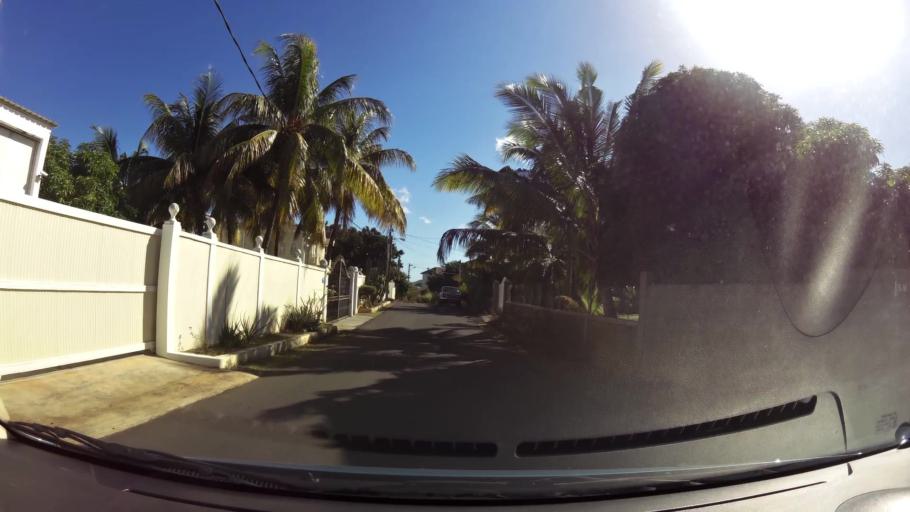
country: MU
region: Black River
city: Flic en Flac
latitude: -20.2696
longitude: 57.3749
